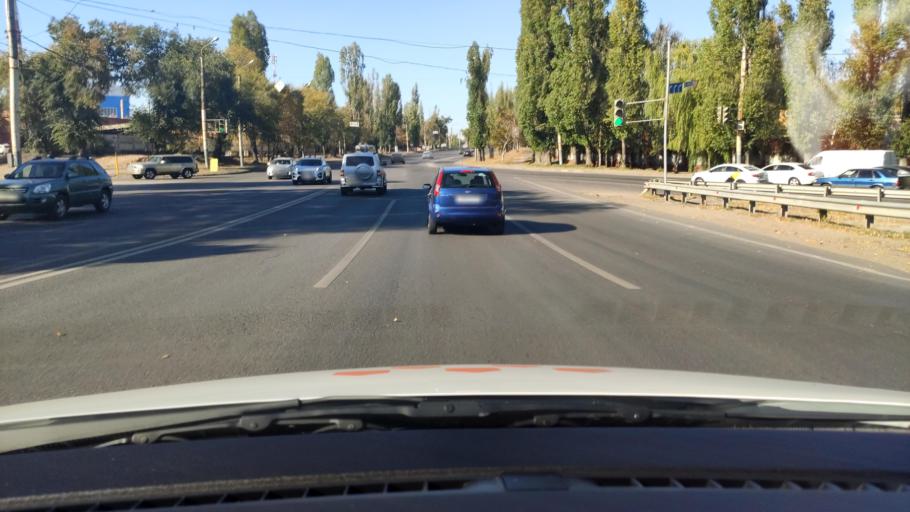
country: RU
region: Voronezj
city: Voronezh
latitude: 51.6236
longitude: 39.2339
